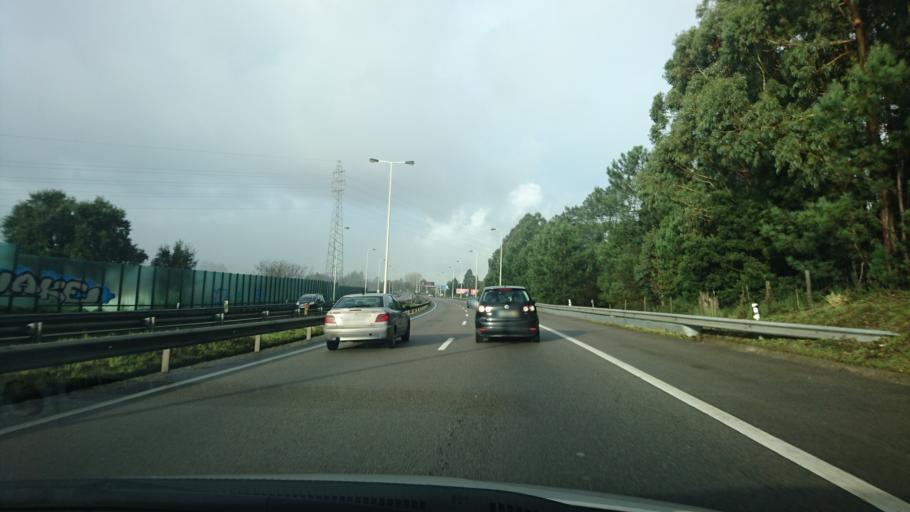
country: PT
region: Porto
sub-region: Gondomar
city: Gondomar
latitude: 41.1545
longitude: -8.5522
